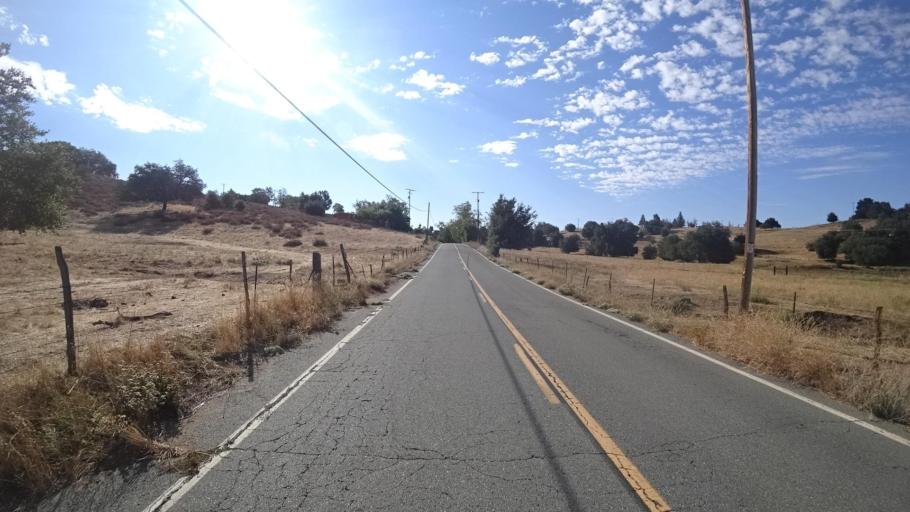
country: US
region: California
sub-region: San Diego County
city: Ramona
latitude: 33.1758
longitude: -116.7655
